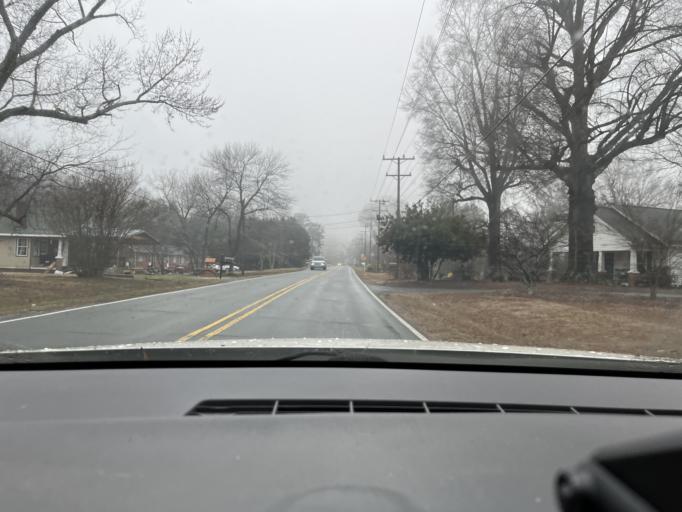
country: US
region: North Carolina
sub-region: Guilford County
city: Pleasant Garden
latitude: 35.9745
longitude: -79.7694
